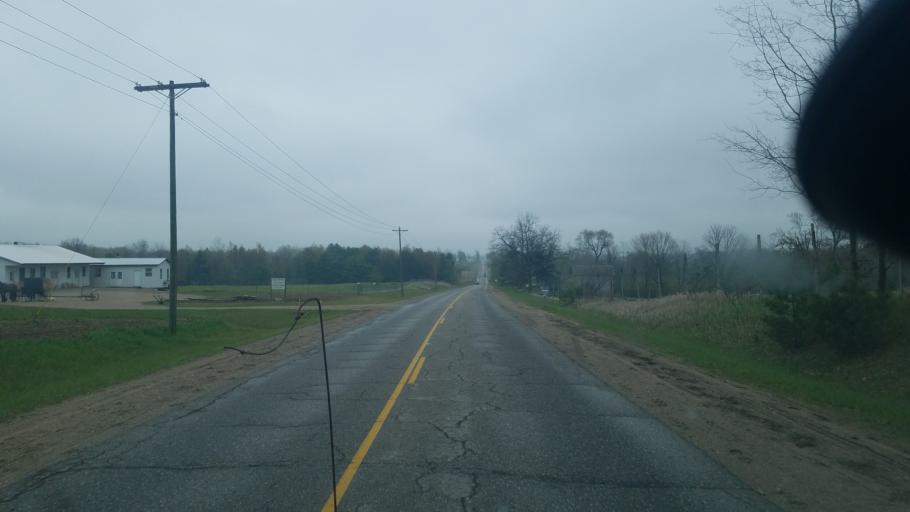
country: US
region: Michigan
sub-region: Mecosta County
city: Canadian Lakes
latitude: 43.5424
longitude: -85.3830
